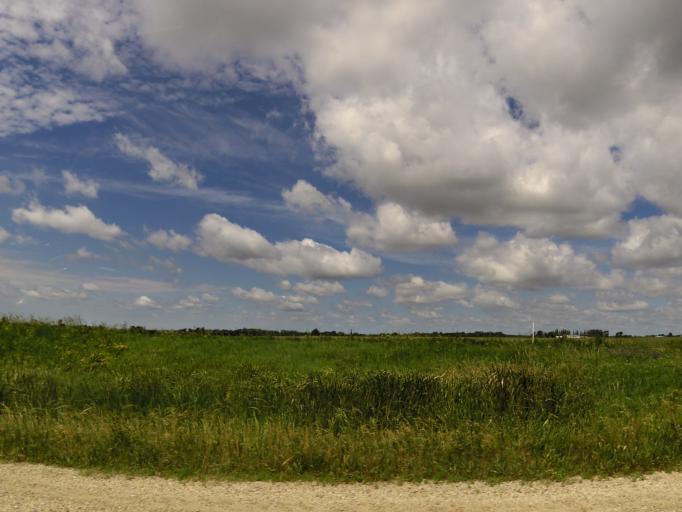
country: US
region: Iowa
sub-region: Chickasaw County
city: New Hampton
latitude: 43.1016
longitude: -92.2979
